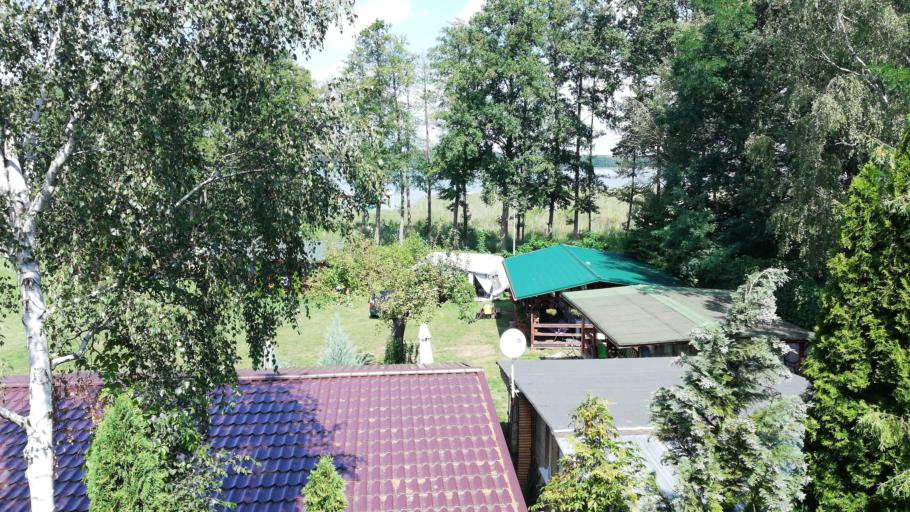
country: PL
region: Lubusz
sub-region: Powiat swiebodzinski
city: Miedzylesie
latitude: 52.2132
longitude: 15.4043
